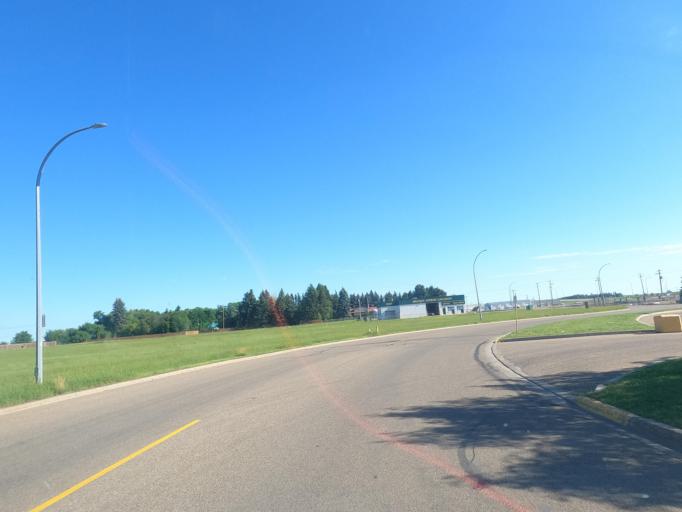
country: CA
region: Alberta
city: Brooks
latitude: 50.5851
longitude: -111.9000
